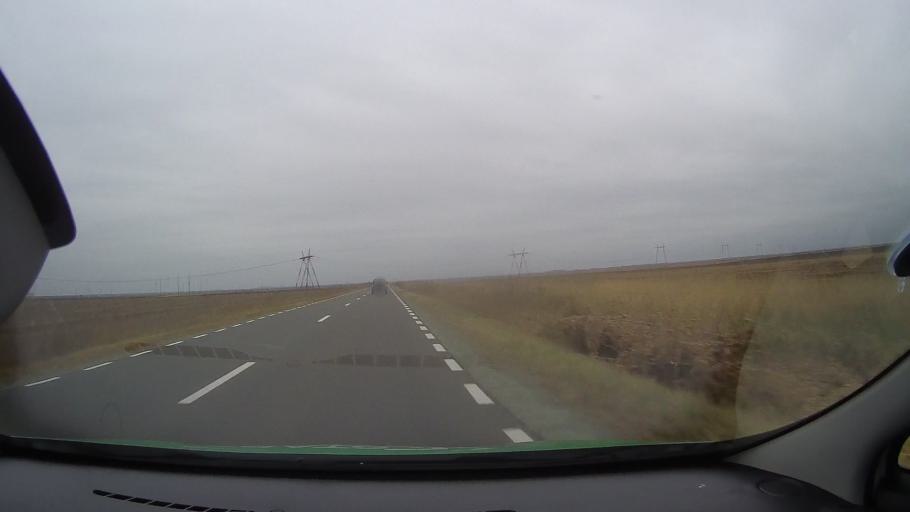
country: RO
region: Ialomita
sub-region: Comuna Gheorghe Lazar
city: Gheorghe Lazar
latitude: 44.6528
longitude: 27.4087
